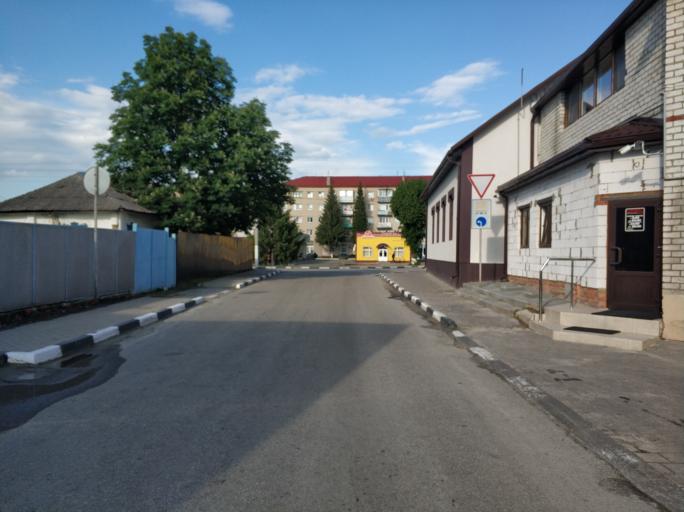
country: RU
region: Belgorod
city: Borisovka
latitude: 50.6085
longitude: 36.0077
